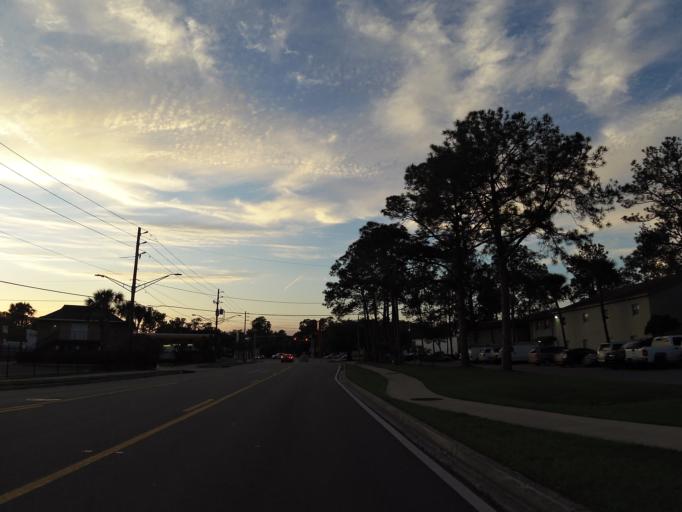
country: US
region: Florida
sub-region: Duval County
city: Jacksonville
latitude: 30.2716
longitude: -81.6074
